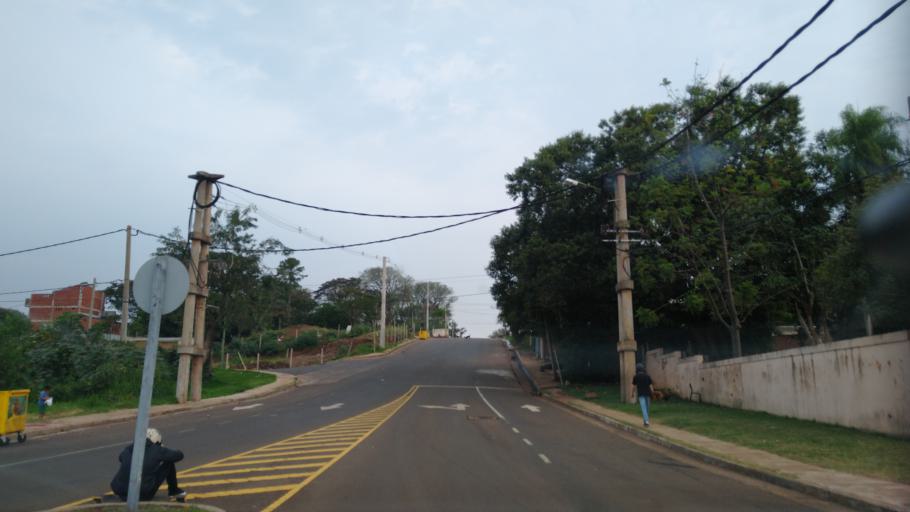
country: AR
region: Misiones
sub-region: Departamento de Capital
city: Posadas
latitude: -27.3550
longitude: -55.9149
